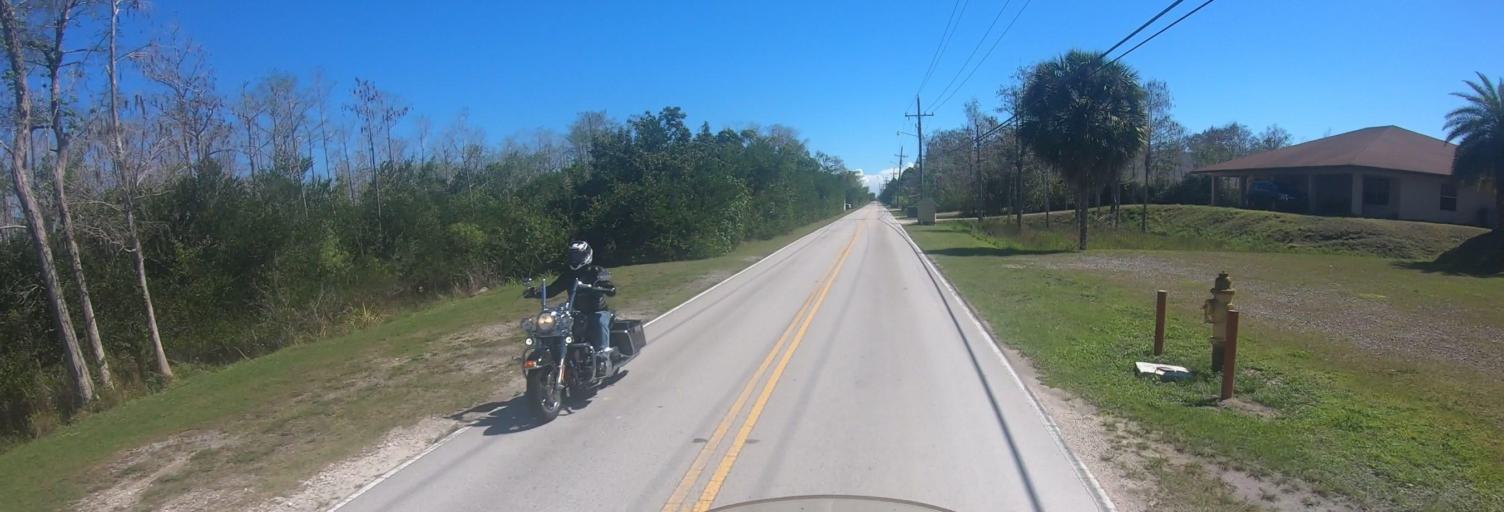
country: US
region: Florida
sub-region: Miami-Dade County
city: Kendall West
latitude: 25.7607
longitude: -80.8350
